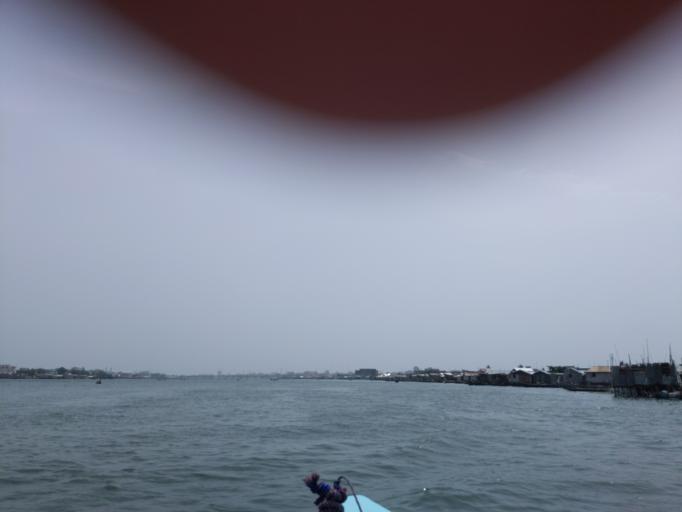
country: BJ
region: Littoral
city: Cotonou
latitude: 6.3874
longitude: 2.4351
